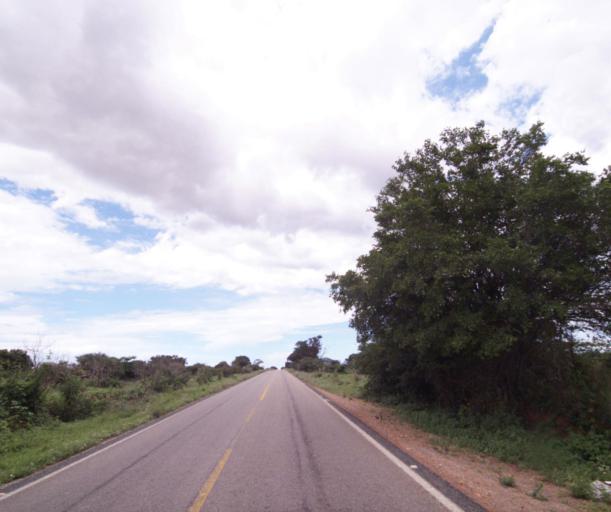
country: BR
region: Bahia
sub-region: Palmas De Monte Alto
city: Palmas de Monte Alto
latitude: -14.2596
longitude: -43.2871
